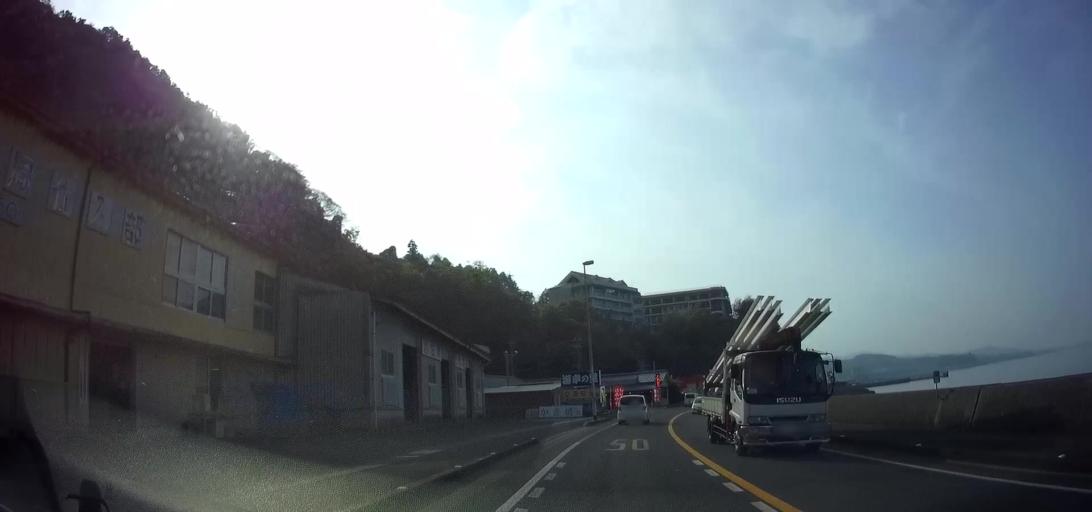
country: JP
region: Nagasaki
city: Shimabara
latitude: 32.7383
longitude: 130.2100
